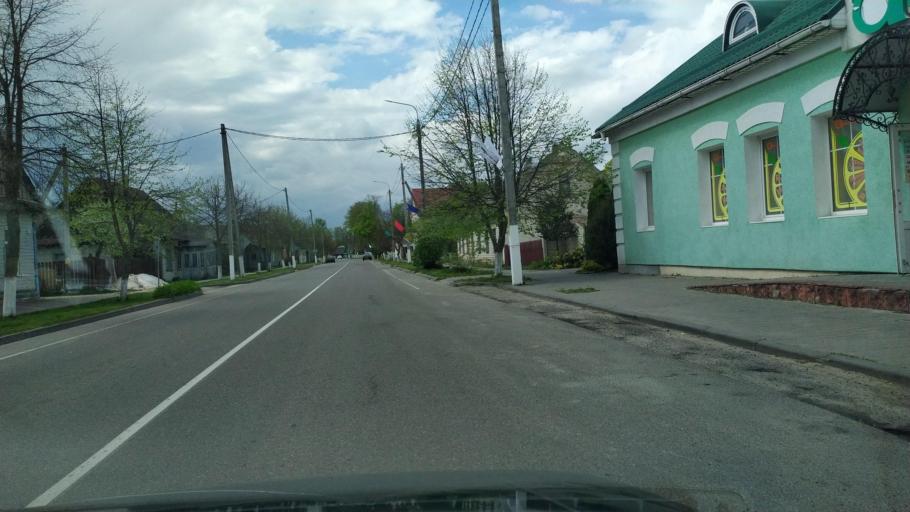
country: BY
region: Brest
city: Pruzhany
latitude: 52.5559
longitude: 24.4548
